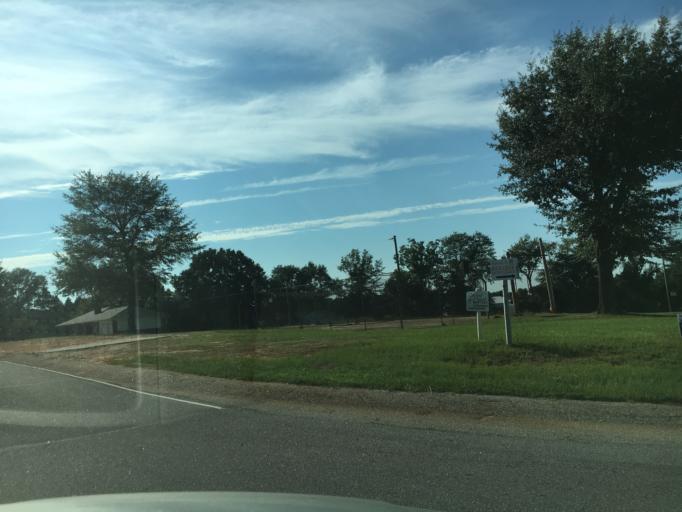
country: US
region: South Carolina
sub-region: Spartanburg County
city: Boiling Springs
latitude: 35.0870
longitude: -81.9293
